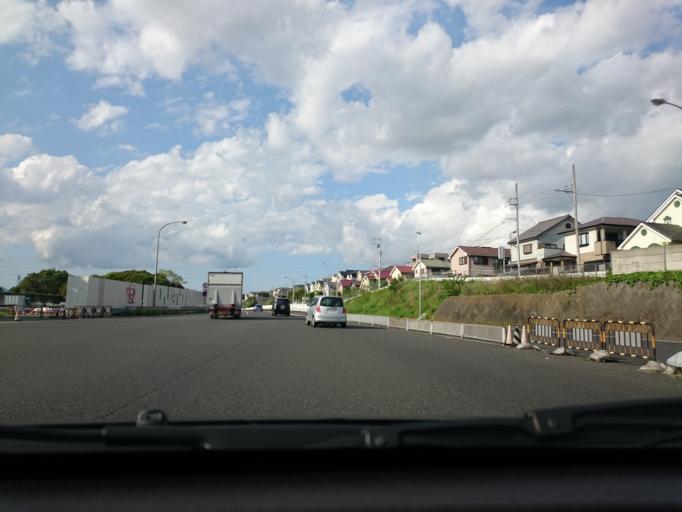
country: JP
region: Kanagawa
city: Oiso
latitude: 35.3376
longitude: 139.2955
